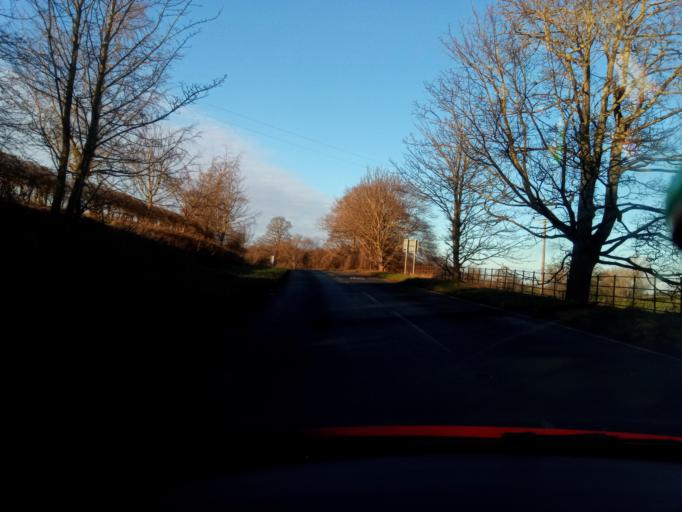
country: GB
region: England
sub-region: North Yorkshire
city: Ripon
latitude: 54.2173
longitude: -1.4552
